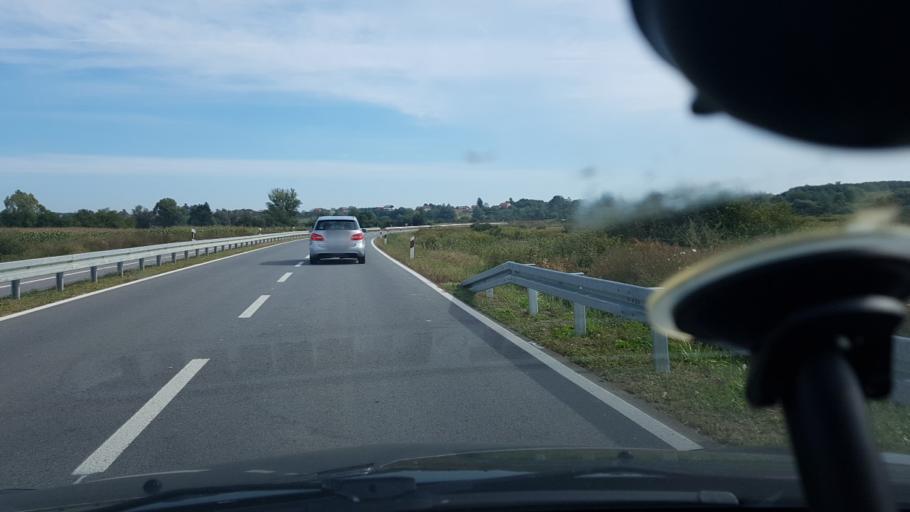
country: HR
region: Krapinsko-Zagorska
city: Marija Bistrica
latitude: 46.0571
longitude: 16.1534
